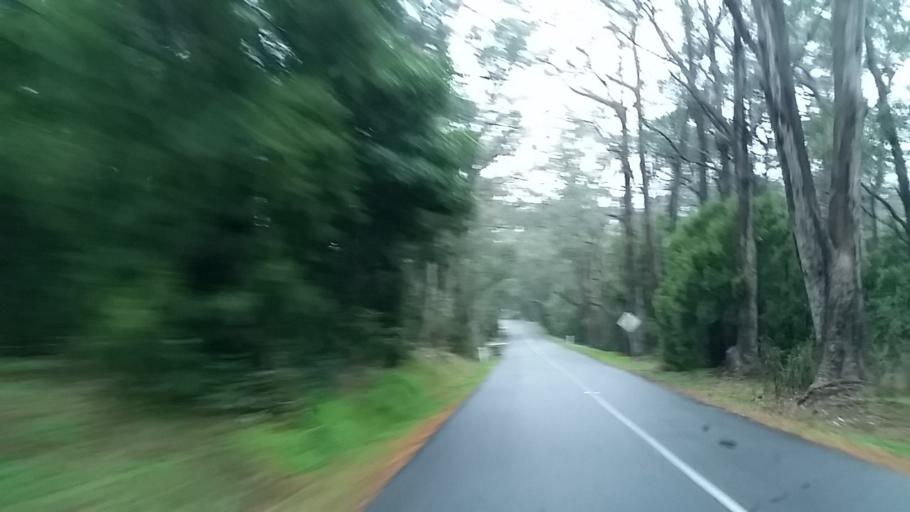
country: AU
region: South Australia
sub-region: Adelaide Hills
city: Adelaide Hills
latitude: -34.9322
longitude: 138.7449
